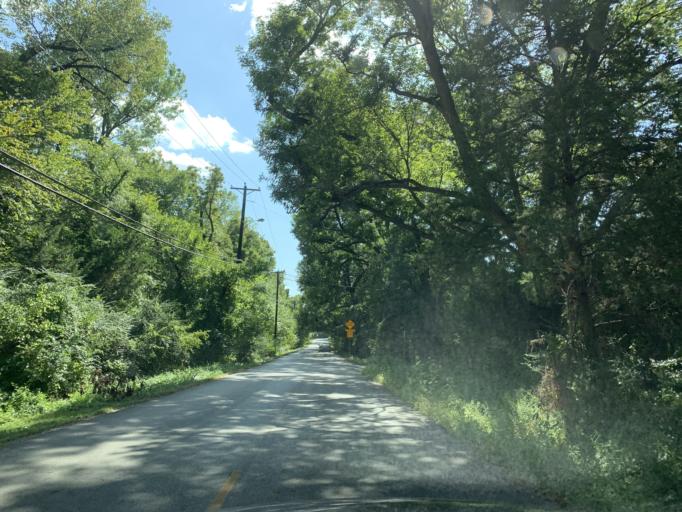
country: US
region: Texas
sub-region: Dallas County
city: Hutchins
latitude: 32.6754
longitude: -96.7718
